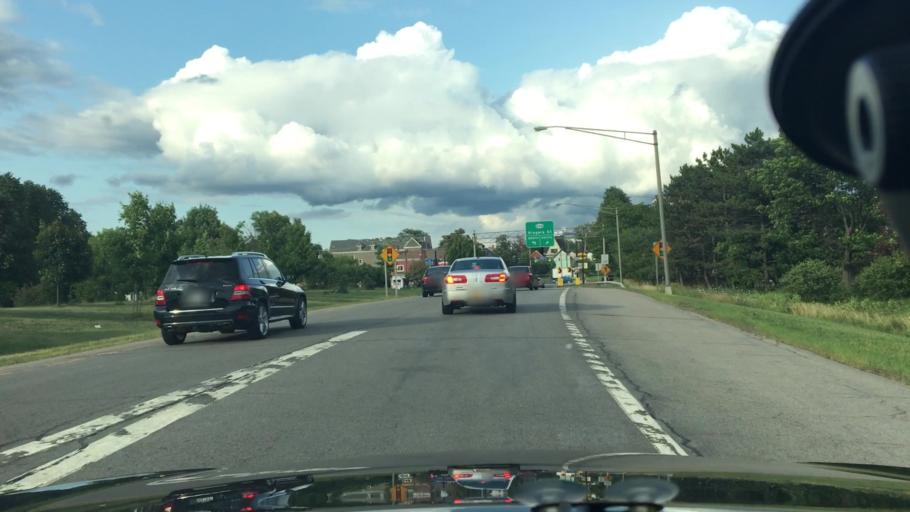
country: US
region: New York
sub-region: Erie County
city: Buffalo
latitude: 42.8919
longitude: -78.8860
